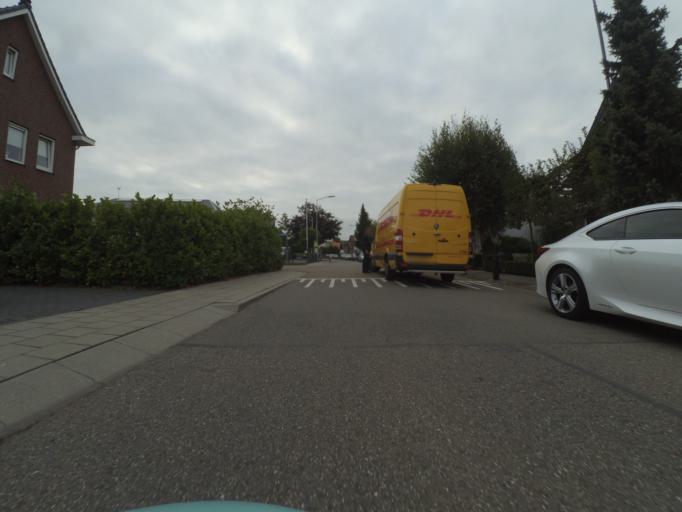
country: NL
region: Utrecht
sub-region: Gemeente Wijk bij Duurstede
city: Wijk bij Duurstede
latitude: 51.9517
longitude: 5.2881
